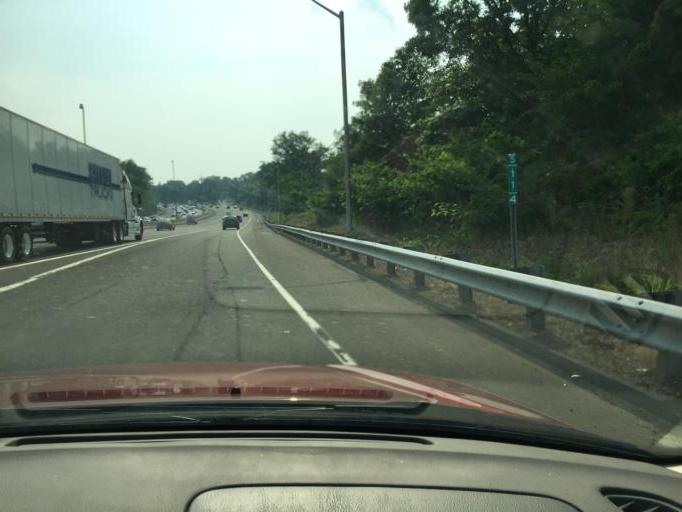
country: US
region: Connecticut
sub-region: Fairfield County
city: Darien
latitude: 41.0719
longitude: -73.4789
